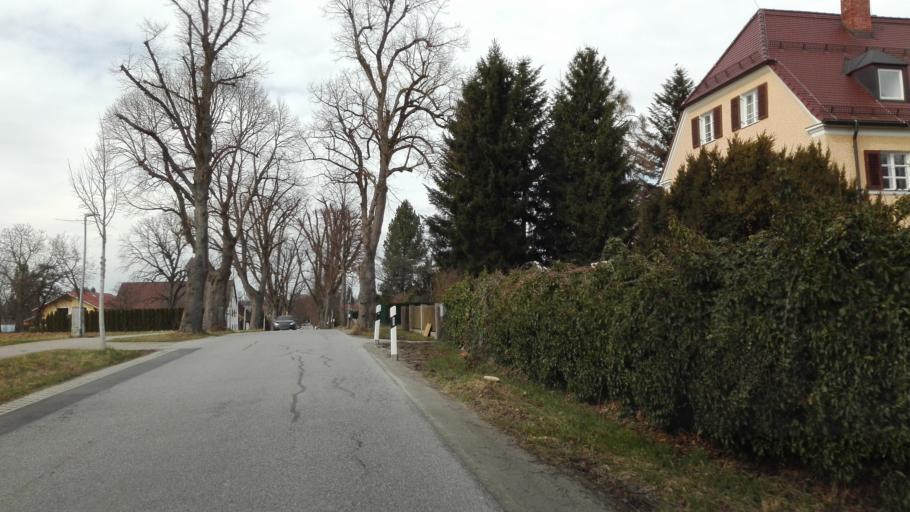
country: DE
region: Bavaria
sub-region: Lower Bavaria
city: Passau
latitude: 48.5626
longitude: 13.4708
